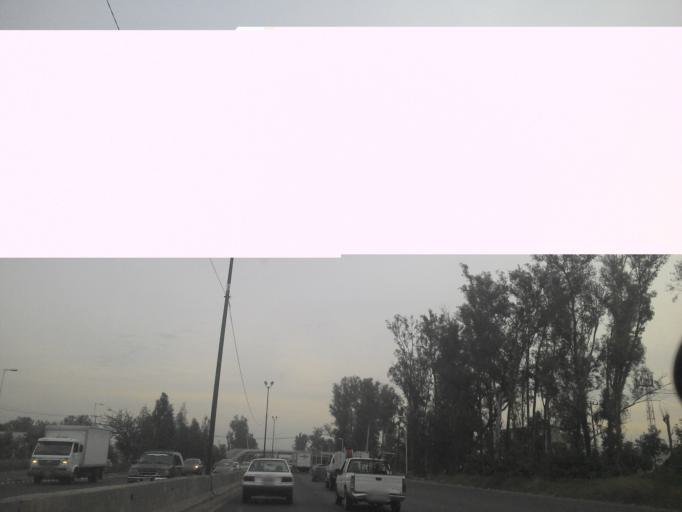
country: MX
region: Jalisco
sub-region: Tlajomulco de Zuniga
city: Palomar
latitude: 20.6405
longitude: -103.4402
